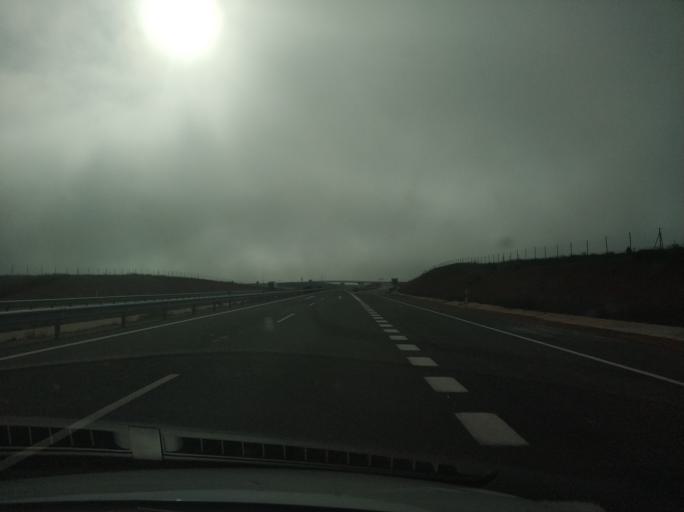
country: ES
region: Castille and Leon
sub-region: Provincia de Soria
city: Alcubilla de las Penas
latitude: 41.2656
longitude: -2.4742
